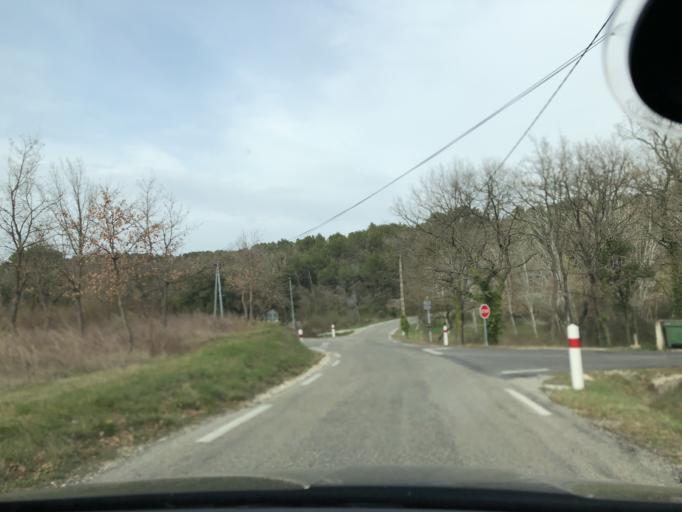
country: FR
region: Provence-Alpes-Cote d'Azur
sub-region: Departement du Vaucluse
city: Menerbes
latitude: 43.8446
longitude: 5.2205
